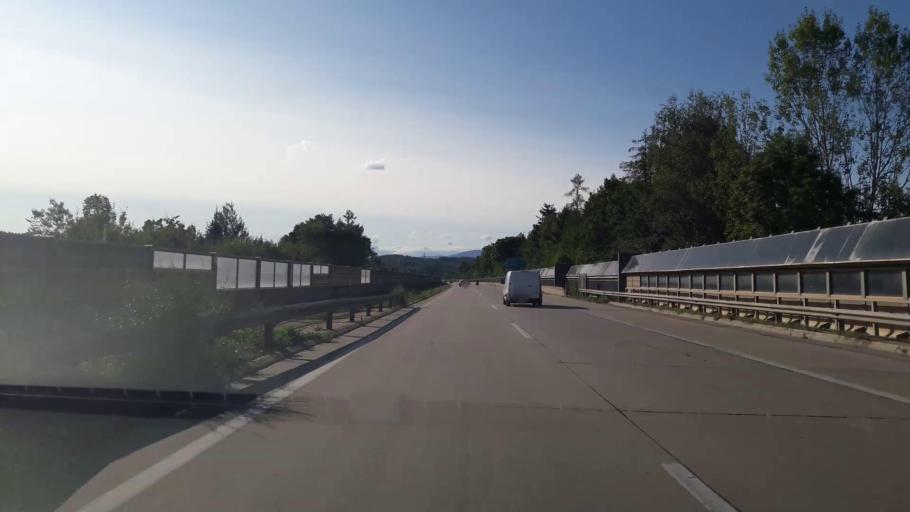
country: AT
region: Styria
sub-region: Politischer Bezirk Weiz
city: Gleisdorf
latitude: 47.0970
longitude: 15.7103
